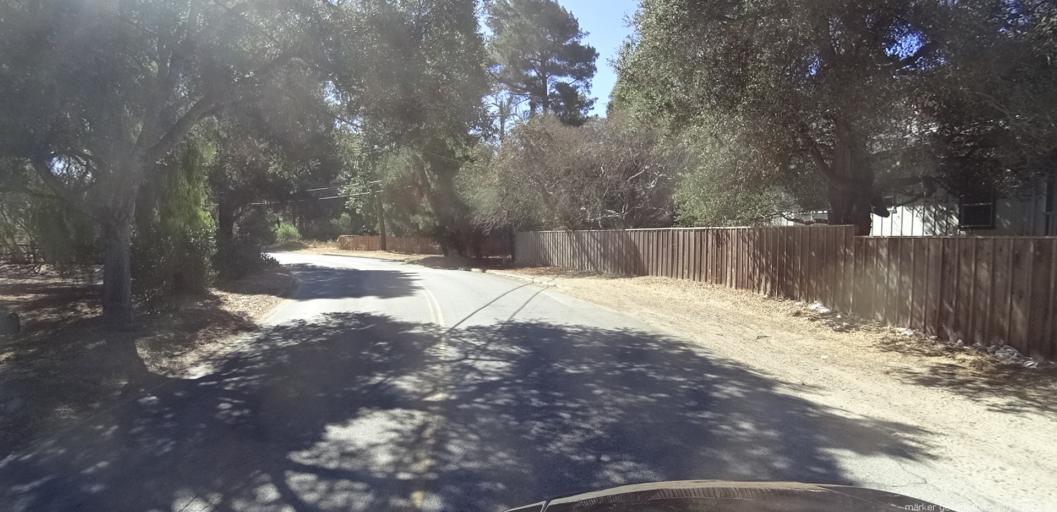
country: US
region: California
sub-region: Monterey County
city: Carmel Valley Village
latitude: 36.4924
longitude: -121.7494
